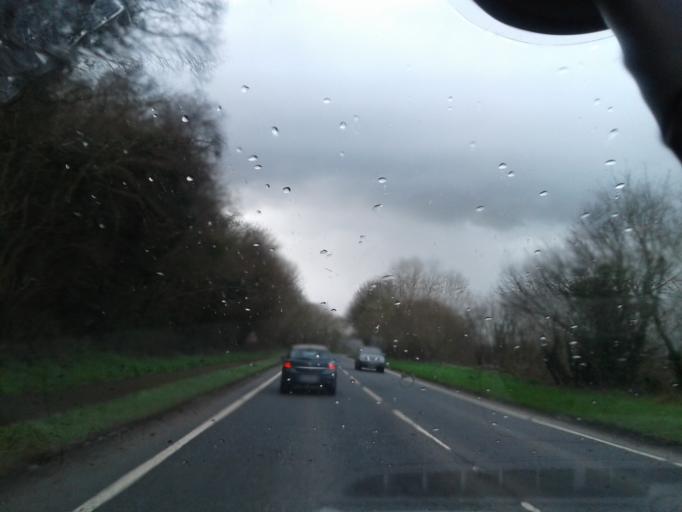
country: GB
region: Northern Ireland
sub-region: Strabane District
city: Sion Mills
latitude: 54.7643
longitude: -7.4650
